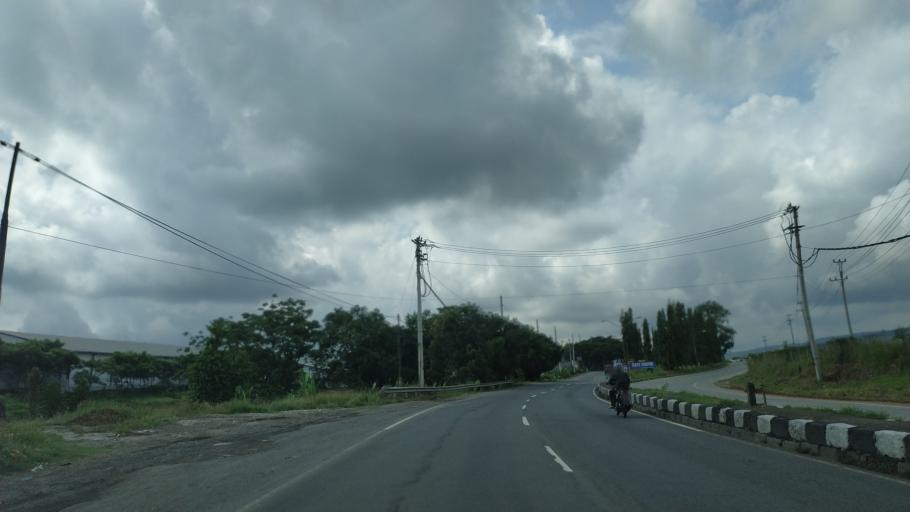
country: ID
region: Central Java
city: Pekalongan
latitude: -6.9469
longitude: 109.8245
